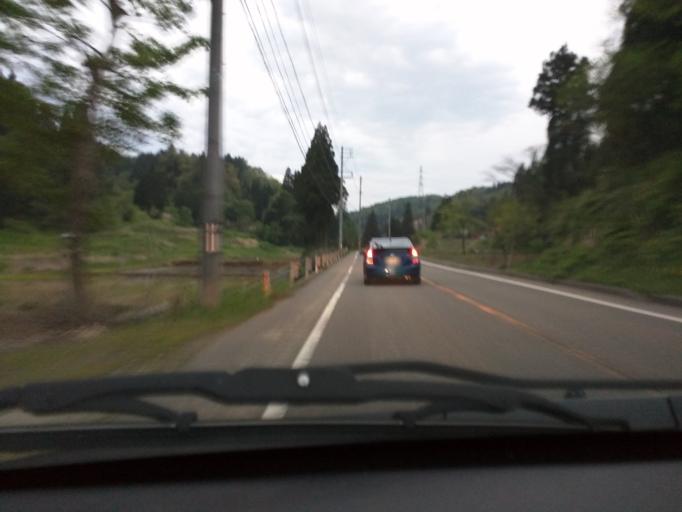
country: JP
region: Niigata
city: Ojiya
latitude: 37.3190
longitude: 138.6994
